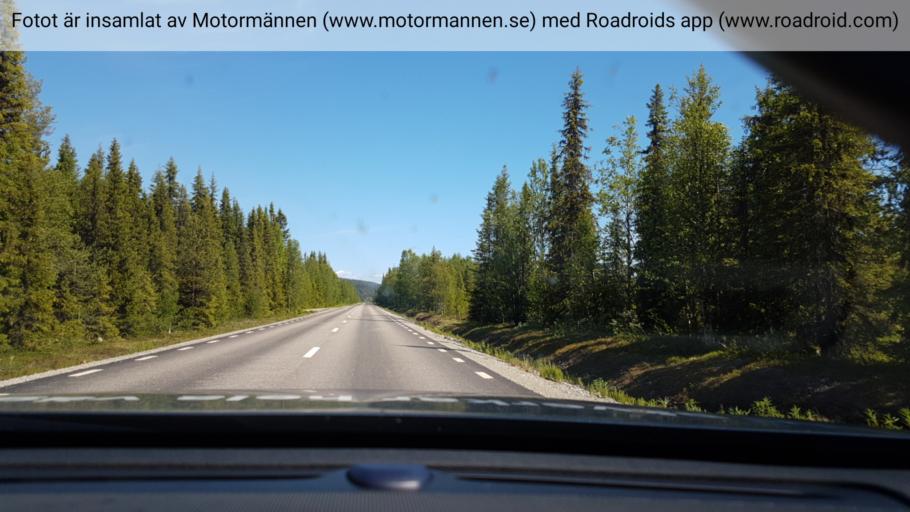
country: SE
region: Vaesterbotten
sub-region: Asele Kommun
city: Insjon
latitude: 64.7249
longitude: 17.5968
